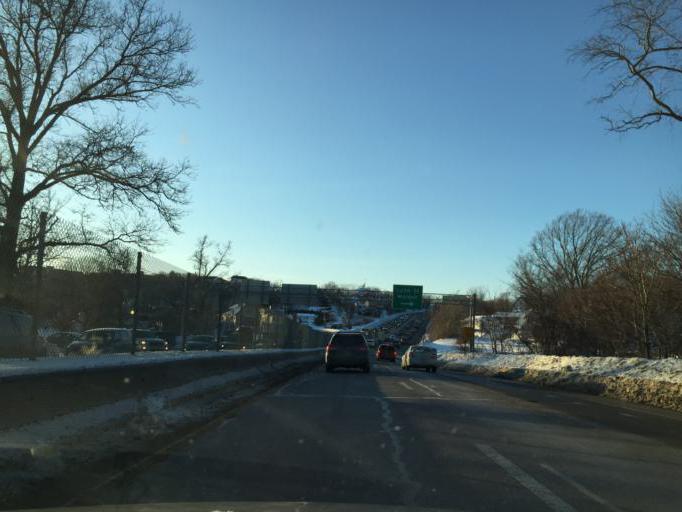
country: US
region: Massachusetts
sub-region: Suffolk County
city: Revere
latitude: 42.4368
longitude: -71.0218
